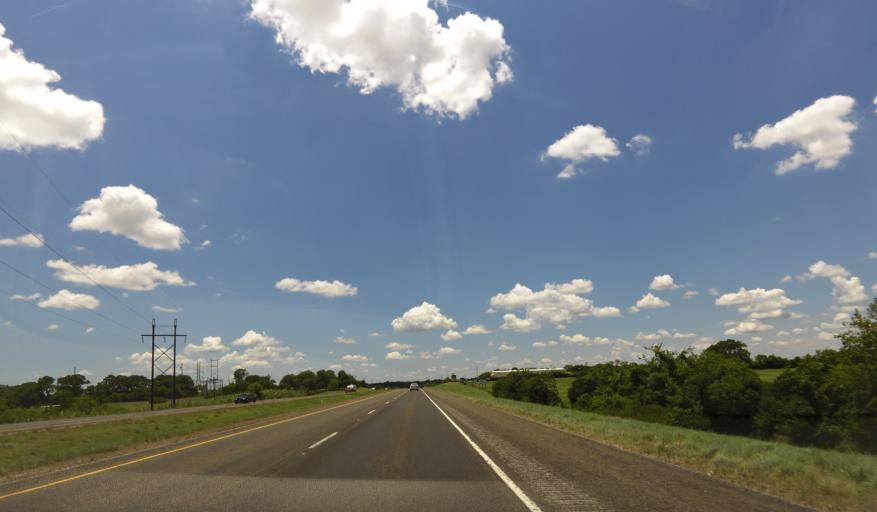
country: US
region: Texas
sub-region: Burleson County
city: Somerville
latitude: 30.1855
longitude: -96.5762
